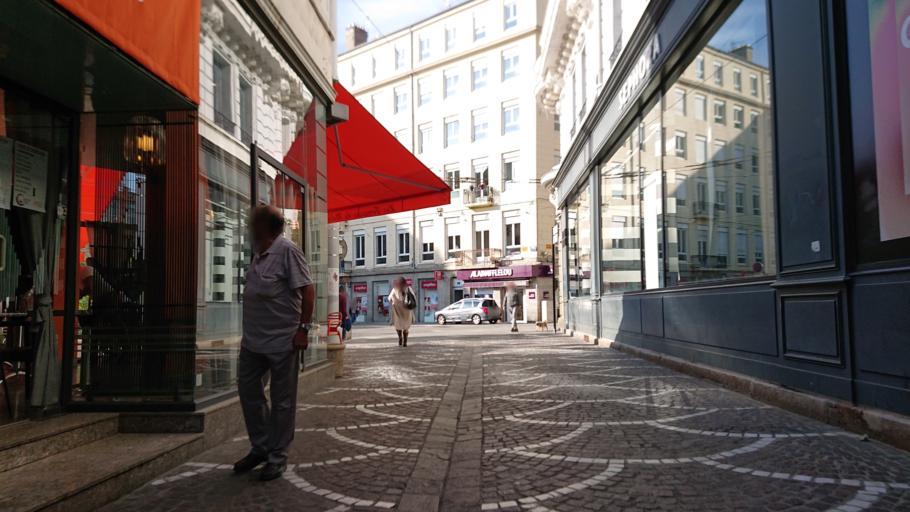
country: FR
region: Rhone-Alpes
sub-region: Departement de la Loire
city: Saint-Etienne
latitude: 45.4384
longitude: 4.3890
